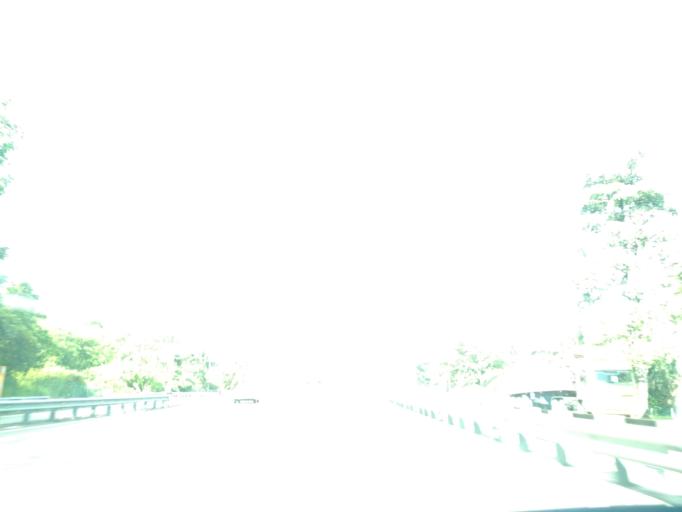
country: MY
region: Penang
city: Bukit Mertajam
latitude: 5.4057
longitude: 100.4840
